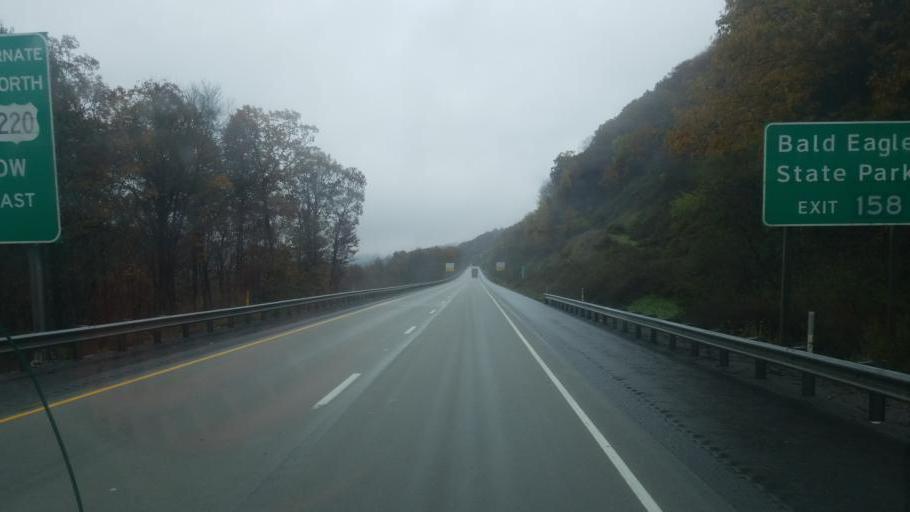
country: US
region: Pennsylvania
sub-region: Centre County
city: Milesburg
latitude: 40.9759
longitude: -77.7952
